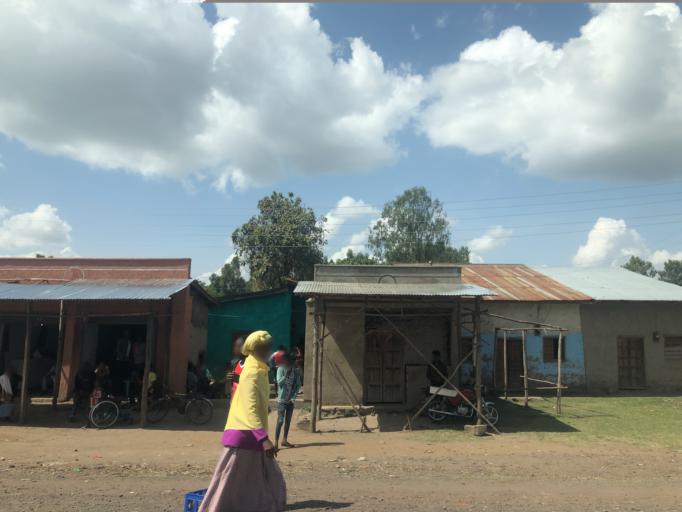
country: ET
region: Southern Nations, Nationalities, and People's Region
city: Boditi
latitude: 7.0326
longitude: 37.9190
